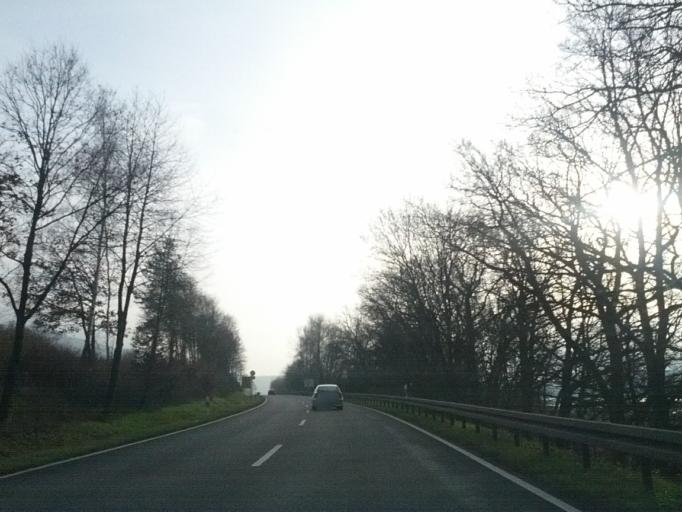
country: DE
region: Thuringia
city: Walldorf
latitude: 50.6278
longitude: 10.3744
